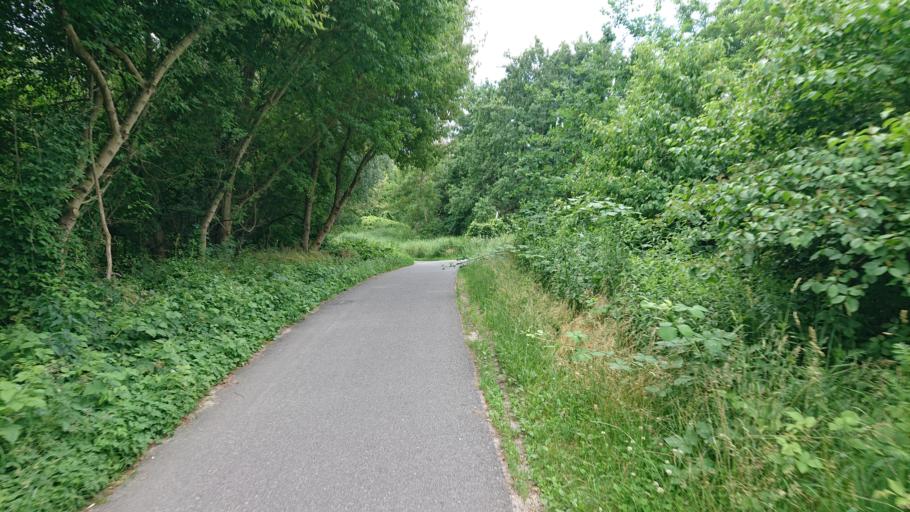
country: DE
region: Brandenburg
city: Potsdam
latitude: 52.3718
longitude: 13.1109
